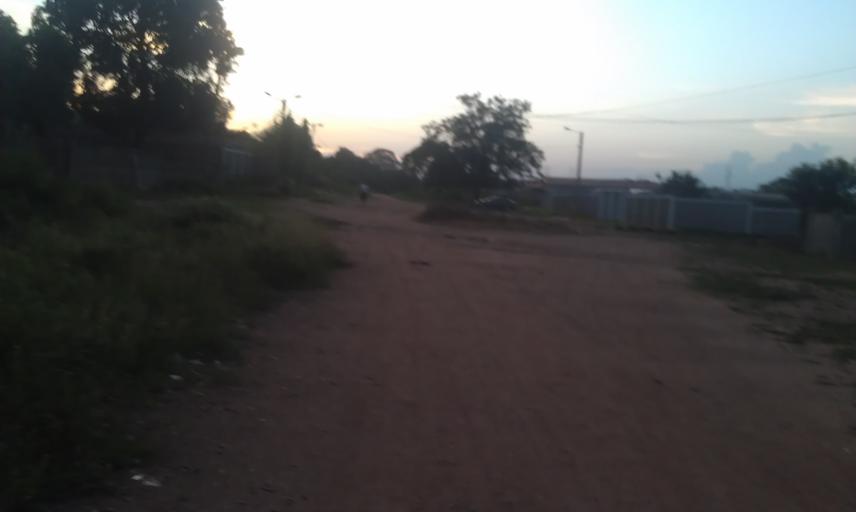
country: CI
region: Vallee du Bandama
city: Bouake
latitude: 7.6931
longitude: -5.0561
